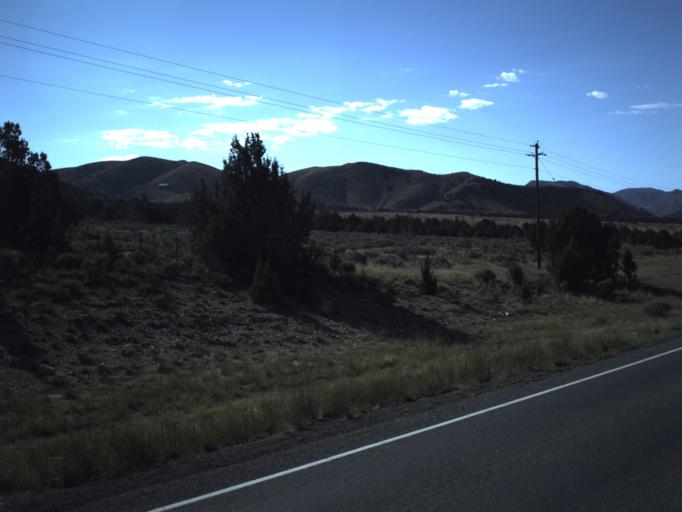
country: US
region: Utah
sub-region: Utah County
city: Genola
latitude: 39.9323
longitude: -112.1492
